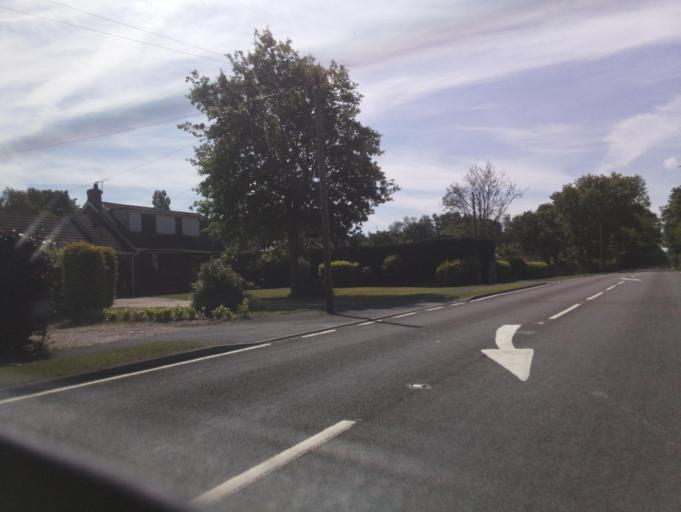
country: GB
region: England
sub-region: North Lincolnshire
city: Manton
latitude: 53.5316
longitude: -0.5775
